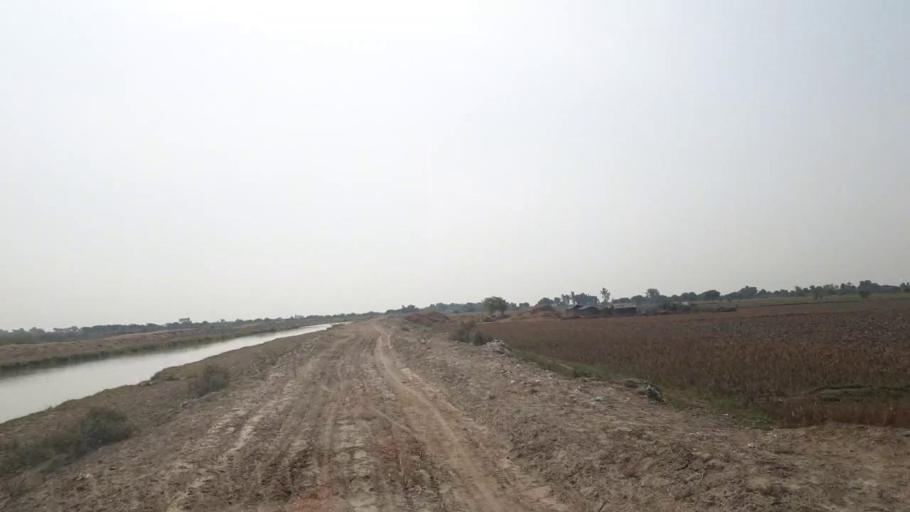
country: PK
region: Sindh
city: Badin
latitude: 24.5485
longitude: 68.8499
